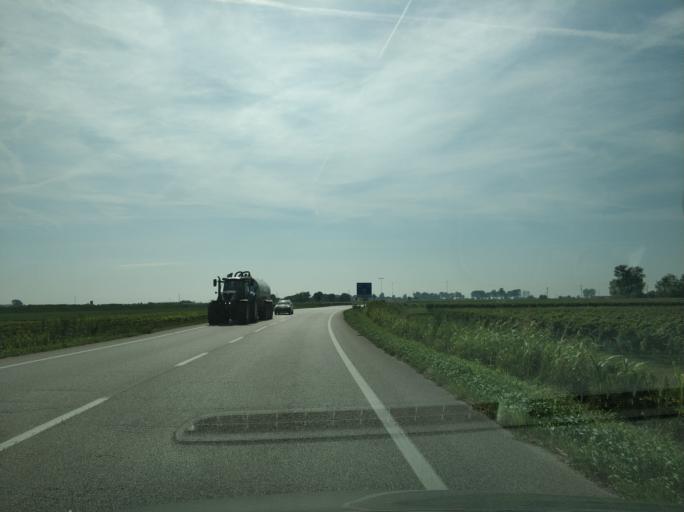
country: IT
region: Veneto
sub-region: Provincia di Padova
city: Correzzola
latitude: 45.2168
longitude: 12.1017
